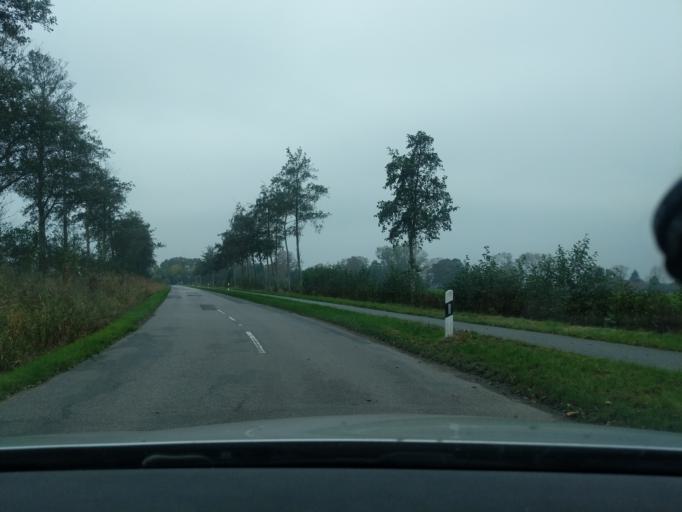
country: DE
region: Lower Saxony
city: Otterndorf
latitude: 53.8187
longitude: 8.8735
